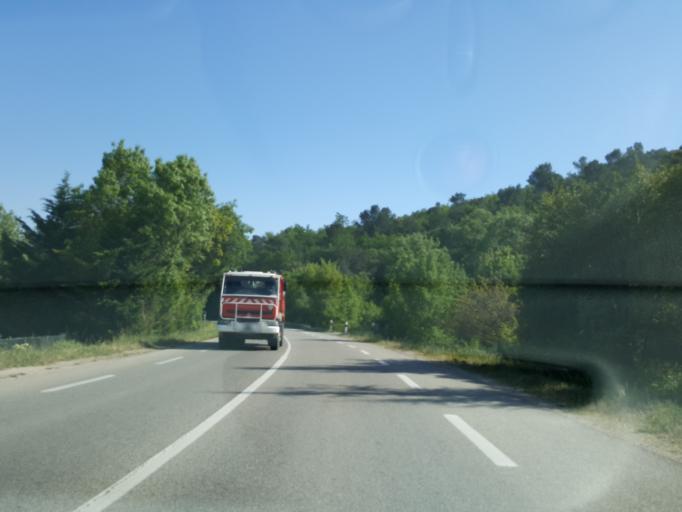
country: FR
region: Provence-Alpes-Cote d'Azur
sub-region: Departement du Var
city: La Roquebrussanne
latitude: 43.3397
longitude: 5.9733
